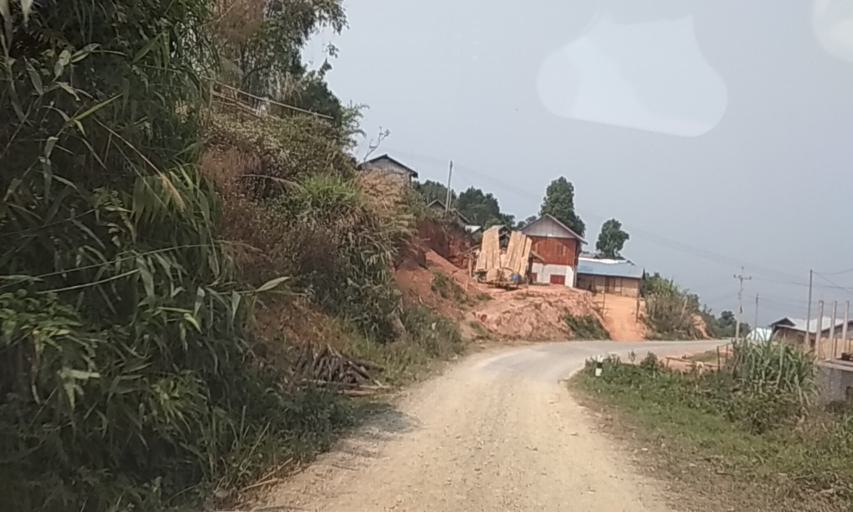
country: TH
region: Nan
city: Chaloem Phra Kiat
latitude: 20.0506
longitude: 101.0700
